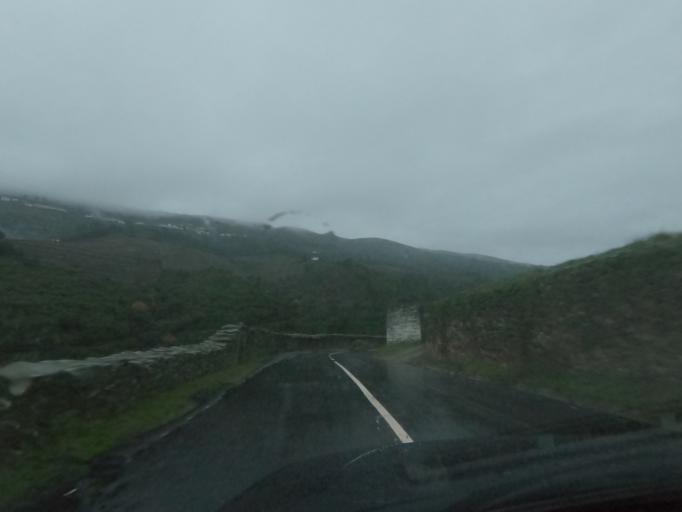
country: PT
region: Vila Real
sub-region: Sabrosa
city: Vilela
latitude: 41.2033
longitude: -7.5625
